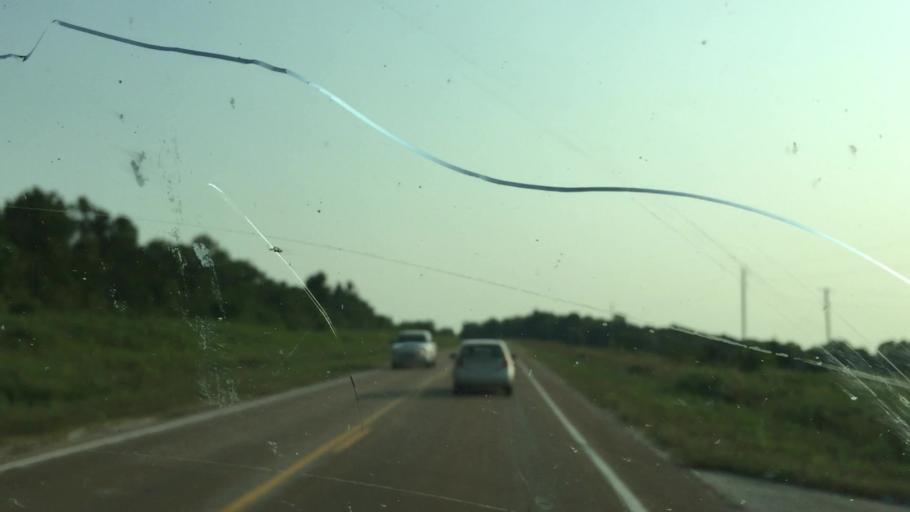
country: US
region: Missouri
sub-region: Pulaski County
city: Richland
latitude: 37.7900
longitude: -92.4083
